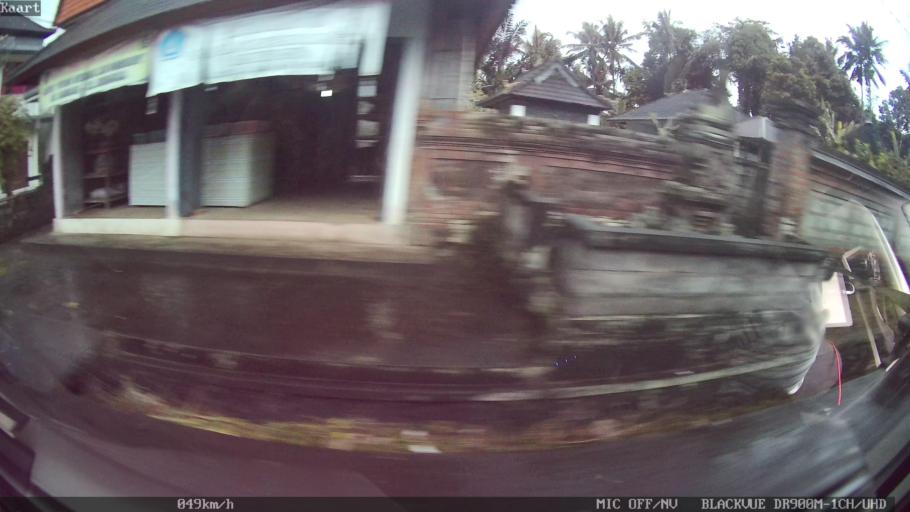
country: ID
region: Bali
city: Banjar Teguan
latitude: -8.5085
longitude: 115.2300
